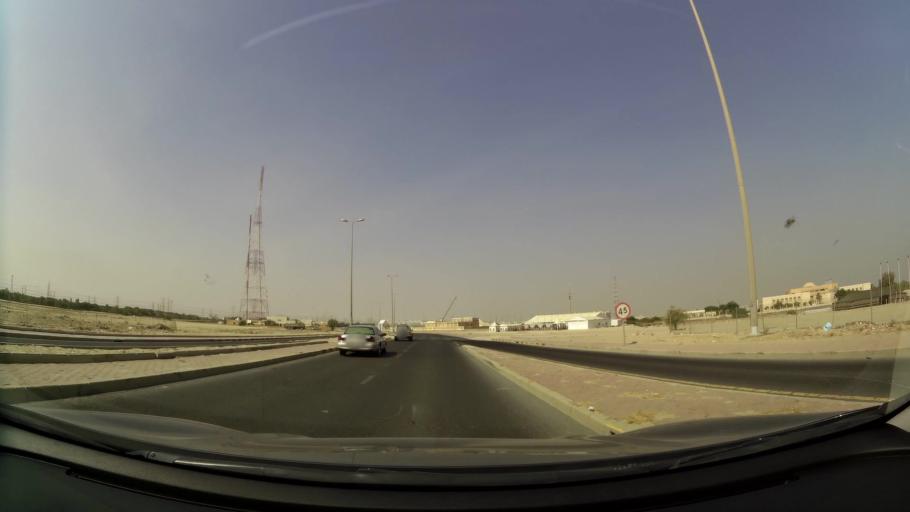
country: KW
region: Al Ahmadi
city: Al Fahahil
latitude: 29.0771
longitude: 48.1080
